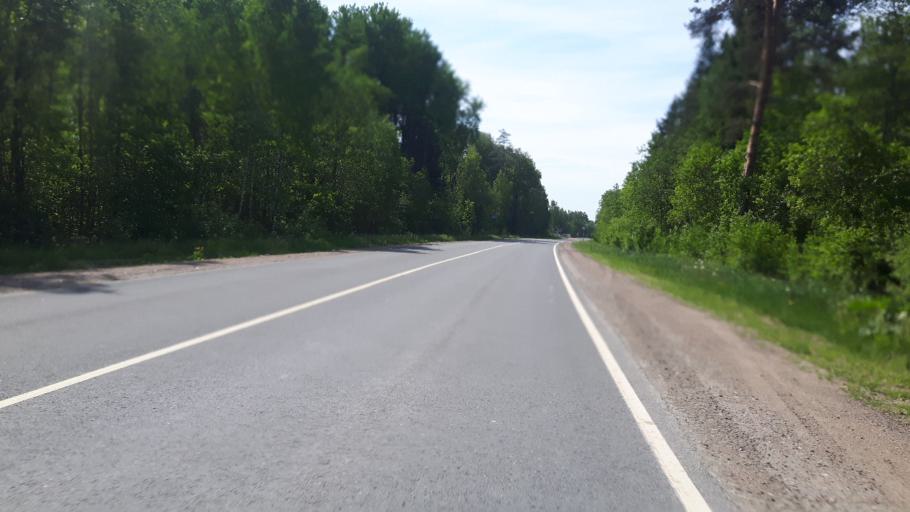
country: RU
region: Leningrad
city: Vistino
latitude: 59.6863
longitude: 28.4602
